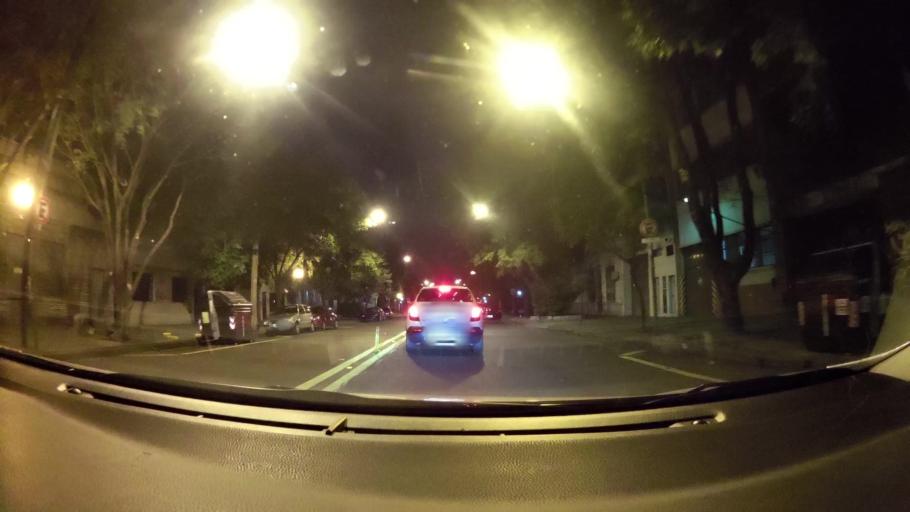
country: AR
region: Buenos Aires F.D.
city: Colegiales
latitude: -34.5825
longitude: -58.4605
